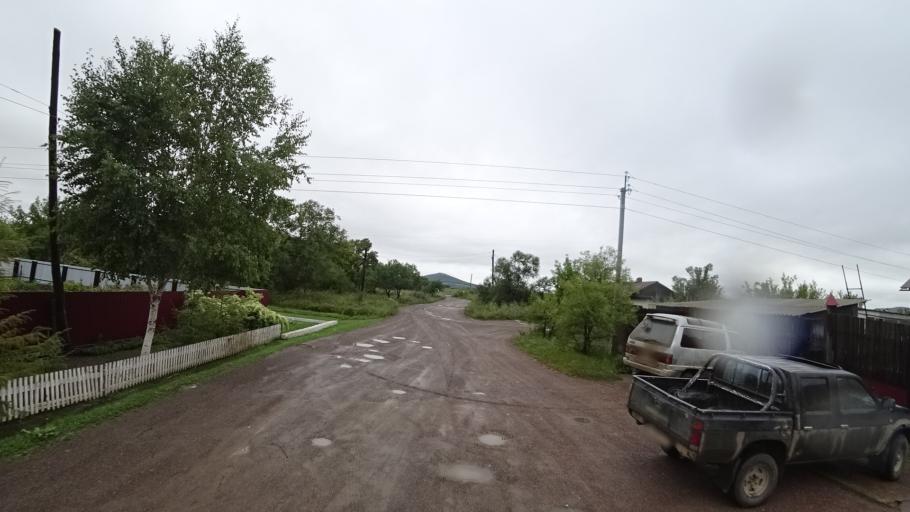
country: RU
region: Primorskiy
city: Monastyrishche
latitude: 44.2287
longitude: 132.4551
